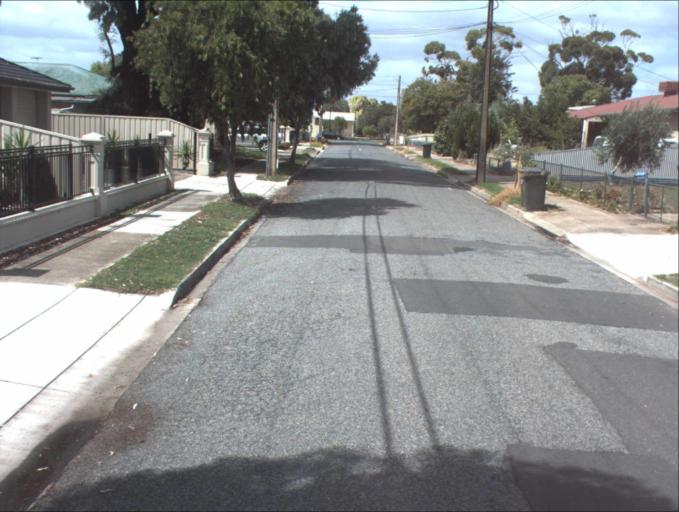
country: AU
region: South Australia
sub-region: Charles Sturt
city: Woodville
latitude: -34.8762
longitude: 138.5628
